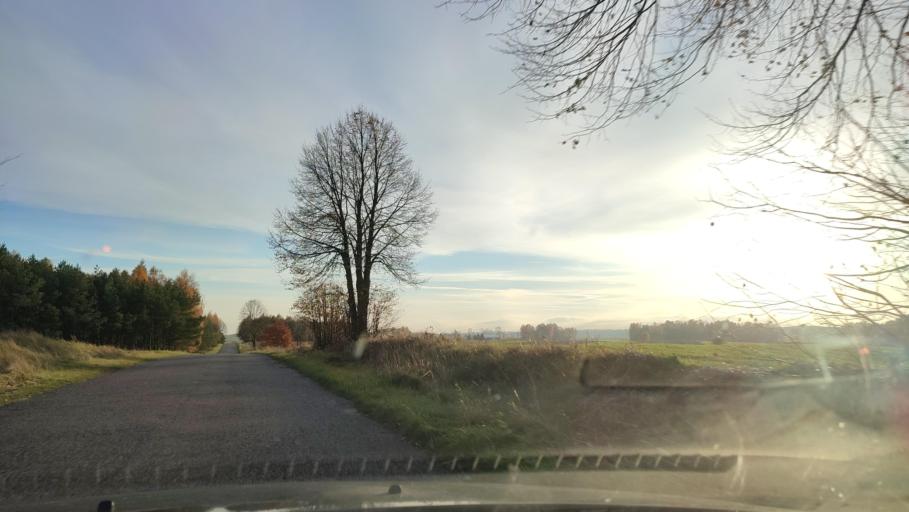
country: PL
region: Masovian Voivodeship
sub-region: Powiat mlawski
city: Dzierzgowo
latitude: 53.2920
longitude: 20.6613
